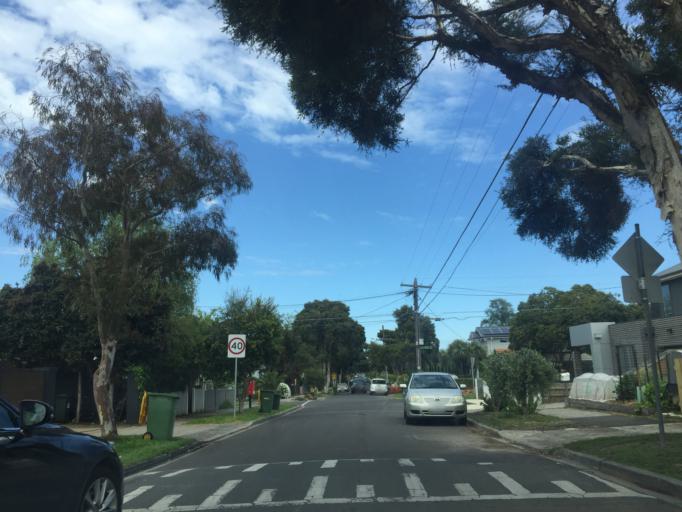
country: AU
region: Victoria
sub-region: Darebin
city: Fairfield
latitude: -37.7726
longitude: 145.0245
